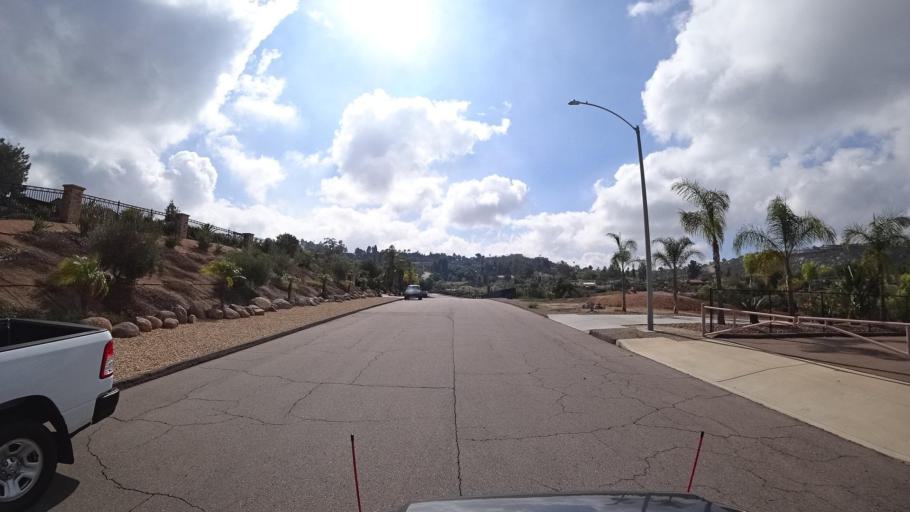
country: US
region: California
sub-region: San Diego County
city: Granite Hills
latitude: 32.7832
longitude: -116.9030
